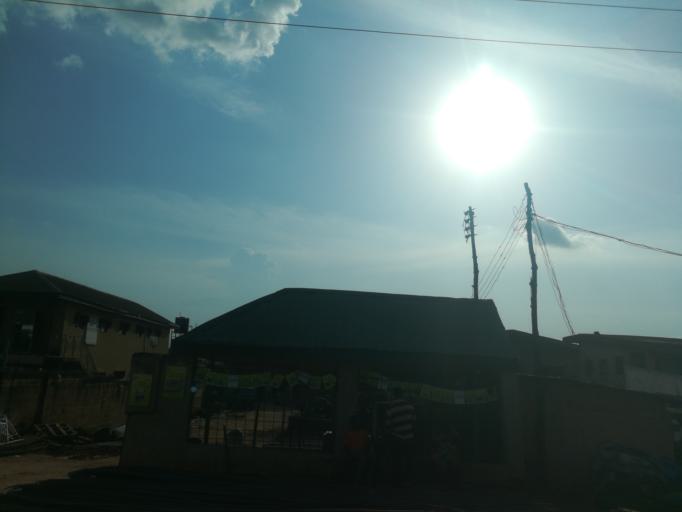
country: NG
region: Oyo
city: Ibadan
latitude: 7.3883
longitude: 3.8224
